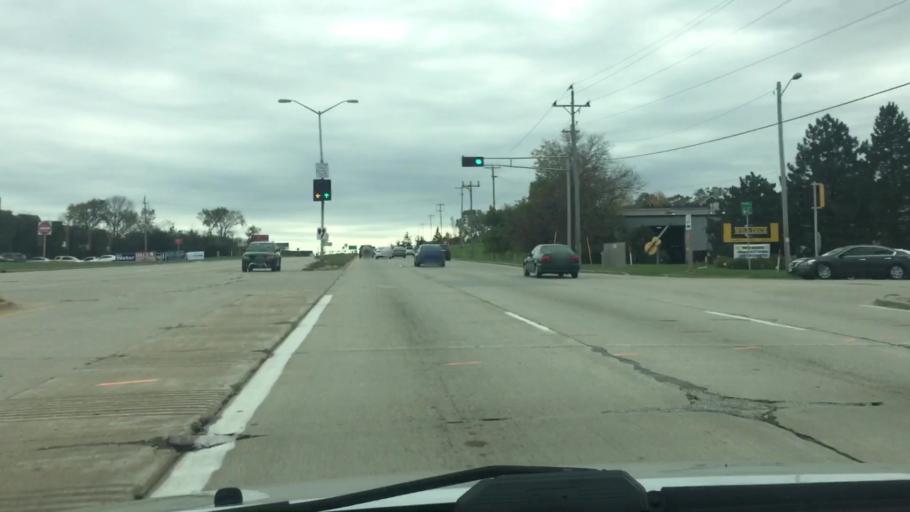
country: US
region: Wisconsin
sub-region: Waukesha County
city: Waukesha
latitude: 43.0080
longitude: -88.1999
